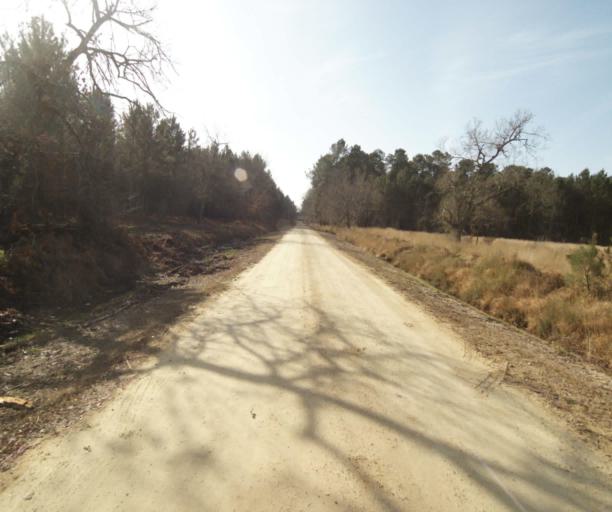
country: FR
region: Aquitaine
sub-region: Departement de la Gironde
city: Grignols
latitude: 44.1955
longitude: -0.1508
